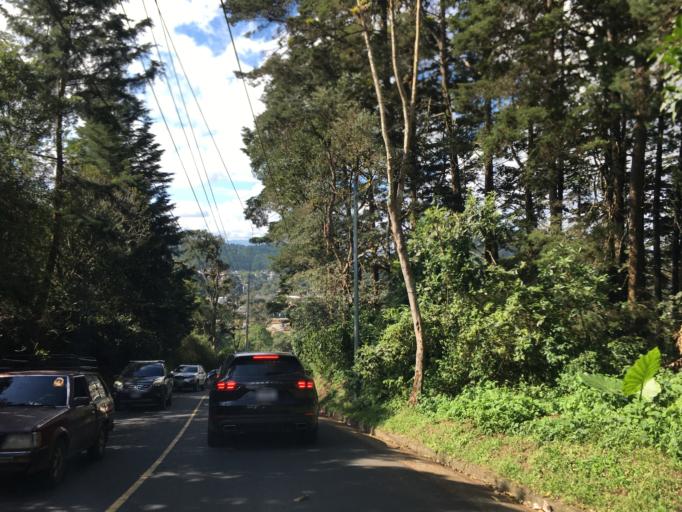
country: GT
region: Guatemala
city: San Jose Pinula
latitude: 14.5700
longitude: -90.4403
